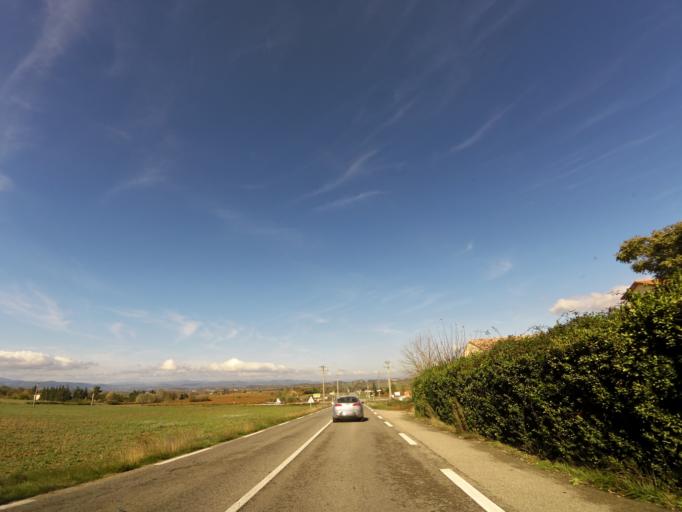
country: FR
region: Languedoc-Roussillon
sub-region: Departement du Gard
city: Ledignan
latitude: 43.9557
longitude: 4.0994
